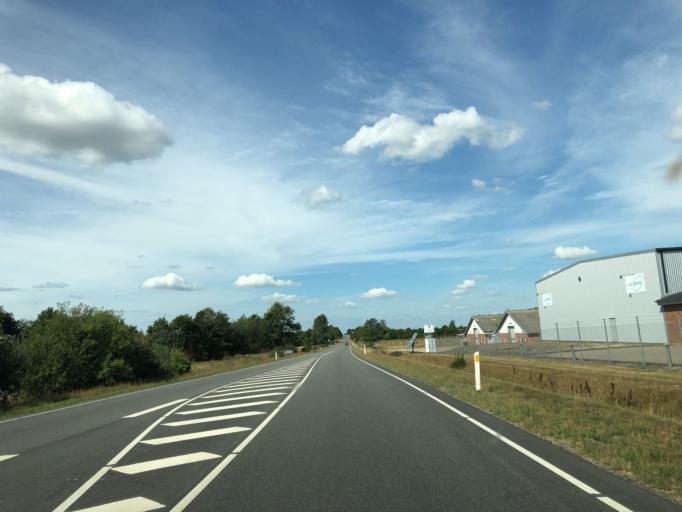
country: DK
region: Central Jutland
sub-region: Ikast-Brande Kommune
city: Bording Kirkeby
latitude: 56.1414
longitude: 9.2637
